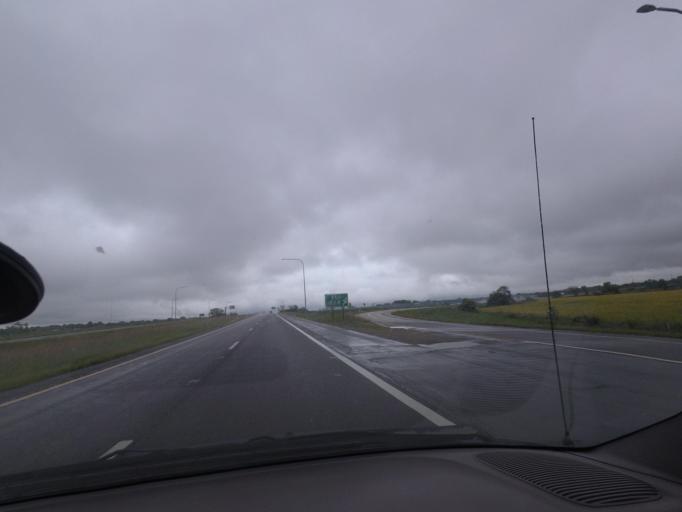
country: US
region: Illinois
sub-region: Champaign County
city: Champaign
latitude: 40.1199
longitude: -88.3094
